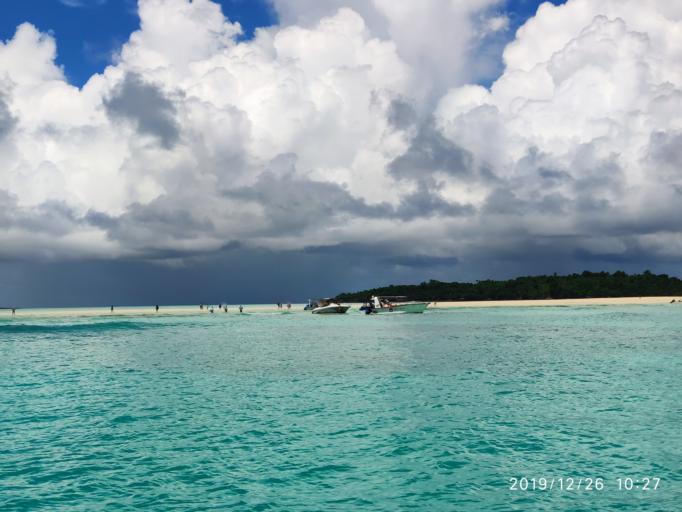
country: MG
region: Diana
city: Hell-Ville
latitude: -13.6049
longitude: 47.8255
